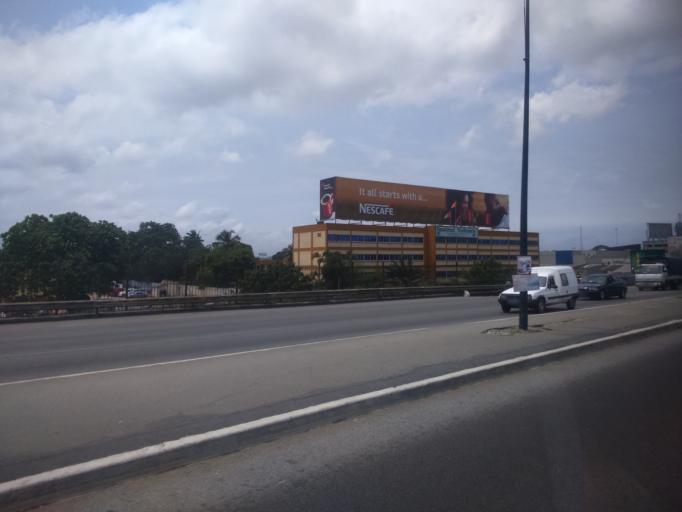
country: CI
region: Lagunes
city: Abidjan
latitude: 5.3041
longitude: -3.9951
